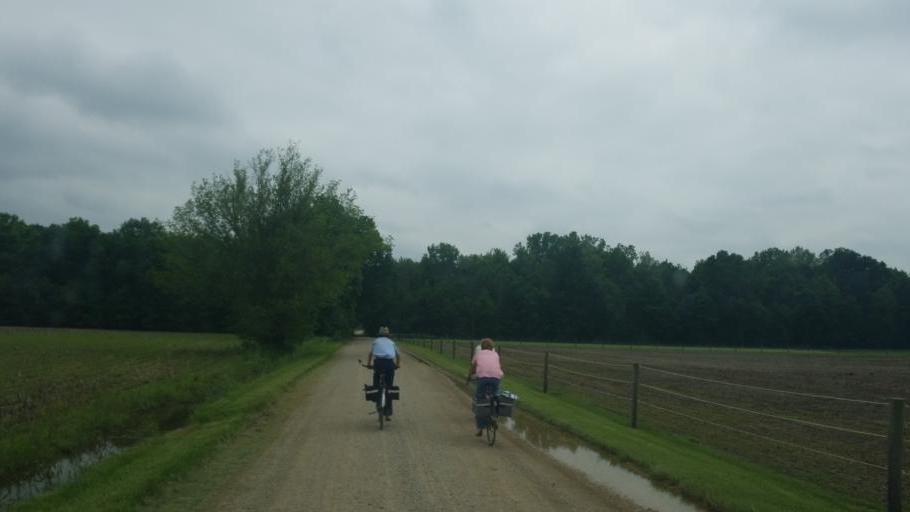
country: US
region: Indiana
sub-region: Elkhart County
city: Nappanee
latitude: 41.4660
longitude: -86.0400
